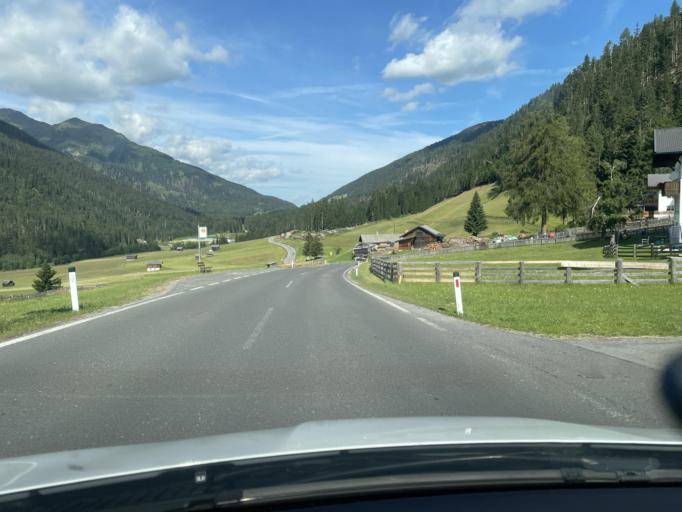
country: AT
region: Tyrol
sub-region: Politischer Bezirk Lienz
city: Obertilliach
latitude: 46.7091
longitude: 12.6059
